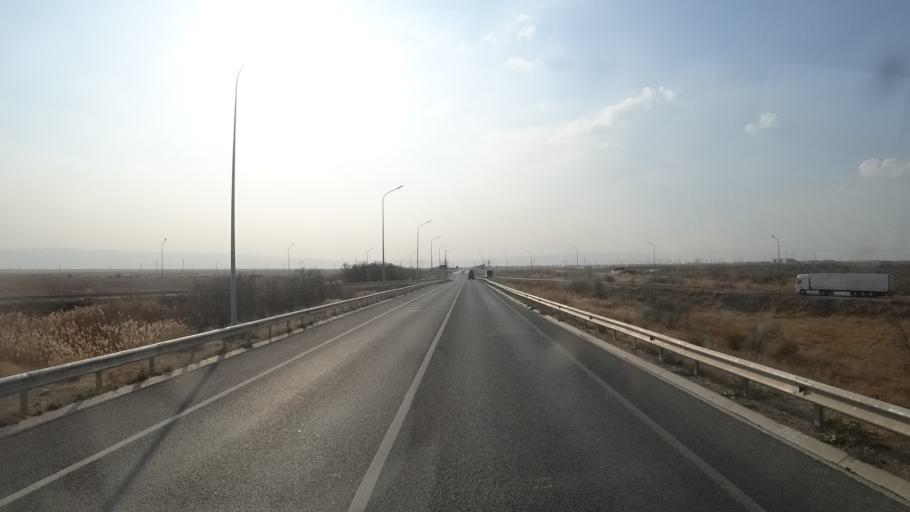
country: KZ
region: Zhambyl
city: Taraz
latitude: 42.8222
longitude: 71.1625
